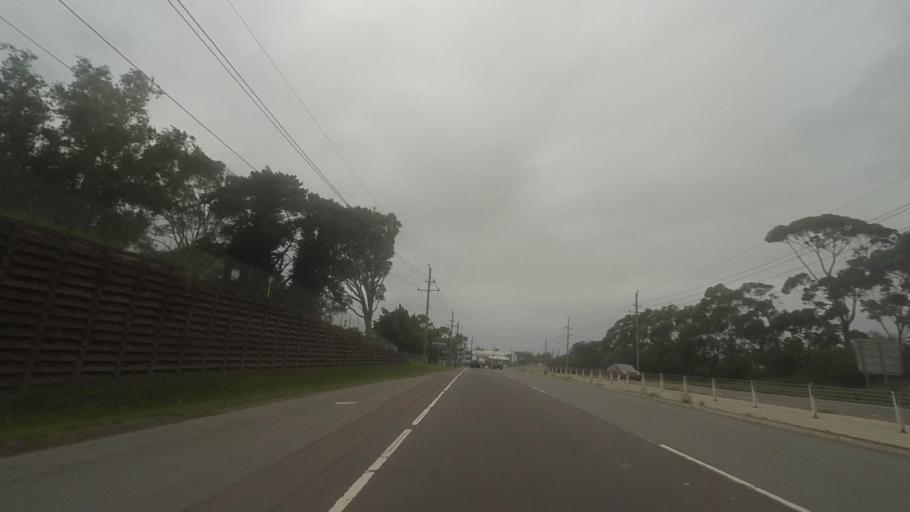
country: AU
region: New South Wales
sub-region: Newcastle
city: Mayfield West
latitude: -32.8791
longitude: 151.7162
